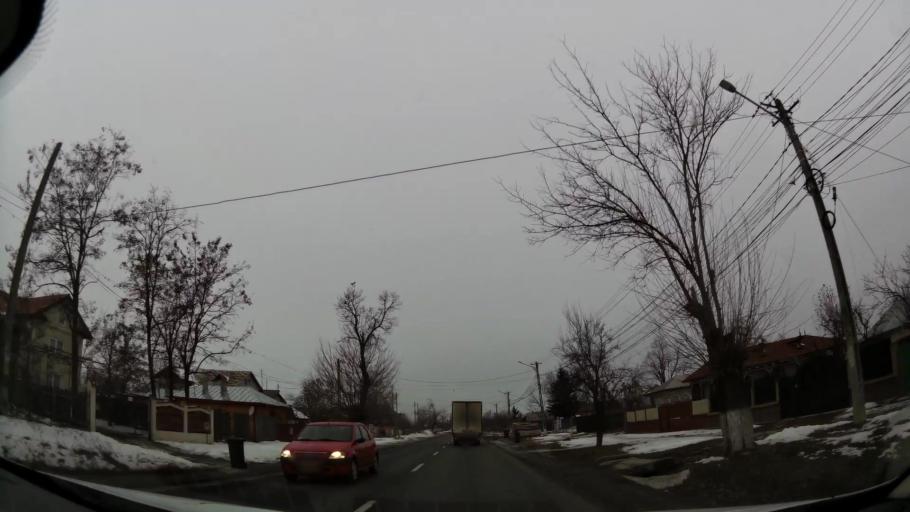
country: RO
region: Dambovita
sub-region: Comuna Tartasesti
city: Baldana
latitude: 44.6173
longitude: 25.7598
